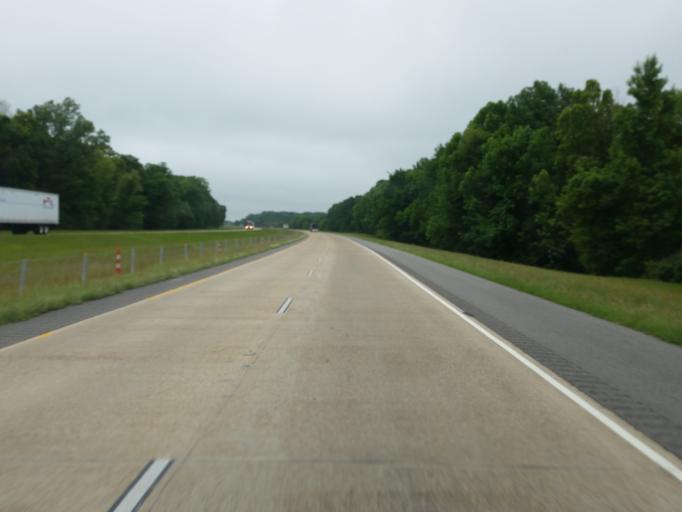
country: US
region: Louisiana
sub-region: Madison Parish
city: Tallulah
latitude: 32.3370
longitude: -91.0635
